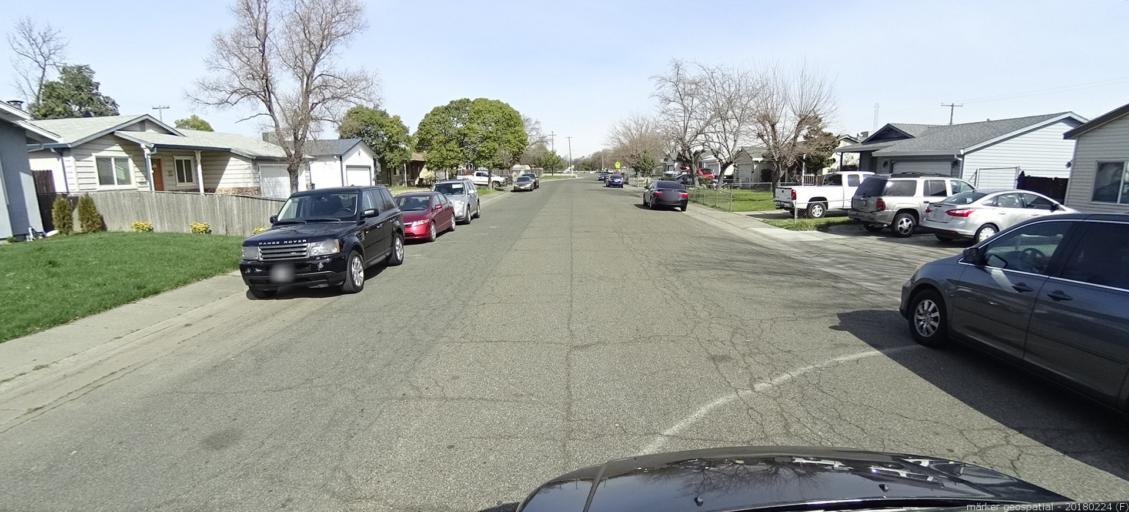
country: US
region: California
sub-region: Sacramento County
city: Rio Linda
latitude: 38.6787
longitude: -121.4431
